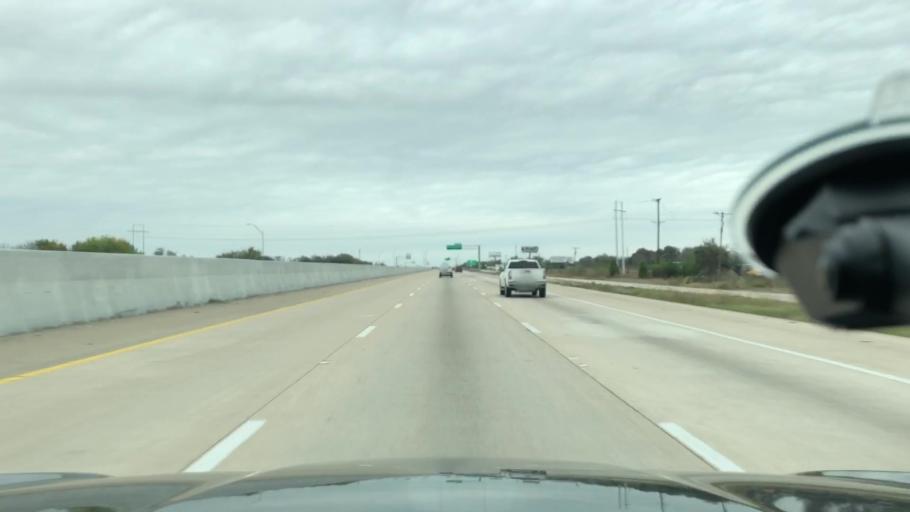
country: US
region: Texas
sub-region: Ellis County
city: Red Oak
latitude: 32.5409
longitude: -96.8221
